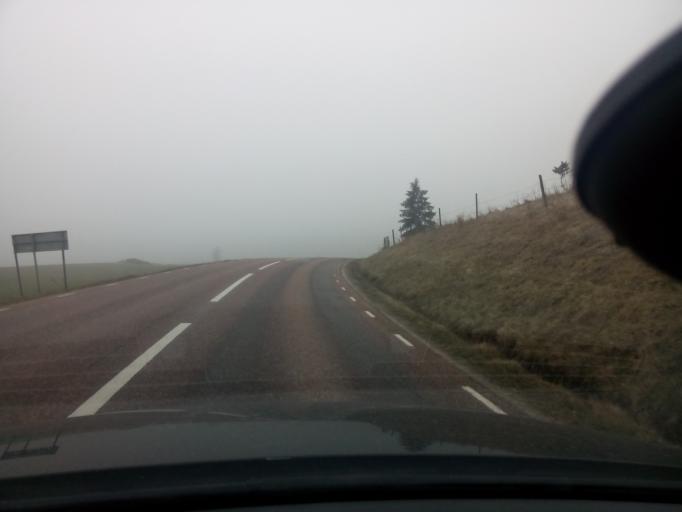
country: SE
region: Soedermanland
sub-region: Nykopings Kommun
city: Nykoping
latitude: 58.8606
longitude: 17.0637
